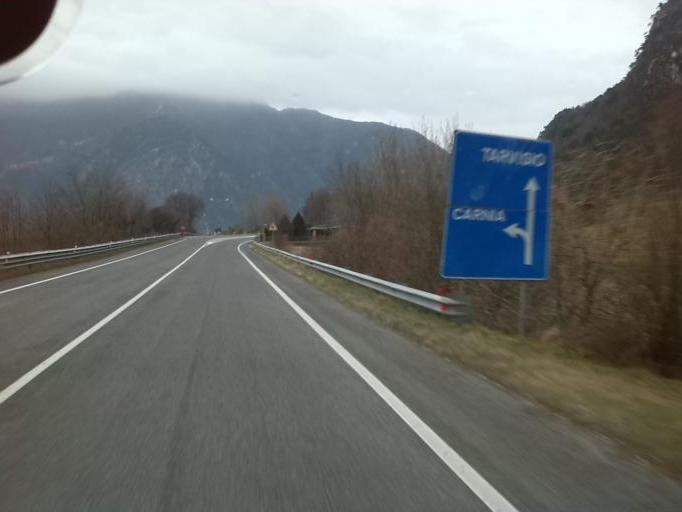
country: IT
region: Friuli Venezia Giulia
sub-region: Provincia di Udine
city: Venzone
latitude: 46.3647
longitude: 13.1350
